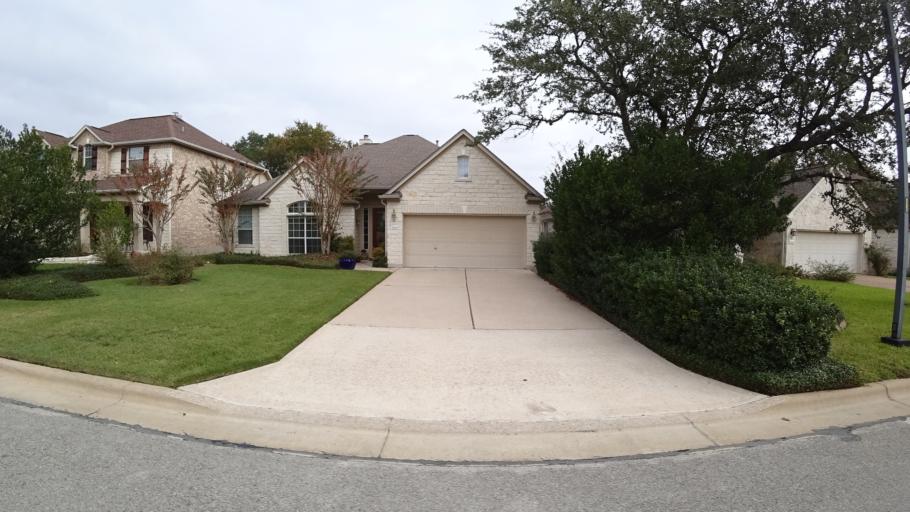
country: US
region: Texas
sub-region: Travis County
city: Shady Hollow
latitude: 30.1985
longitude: -97.8961
